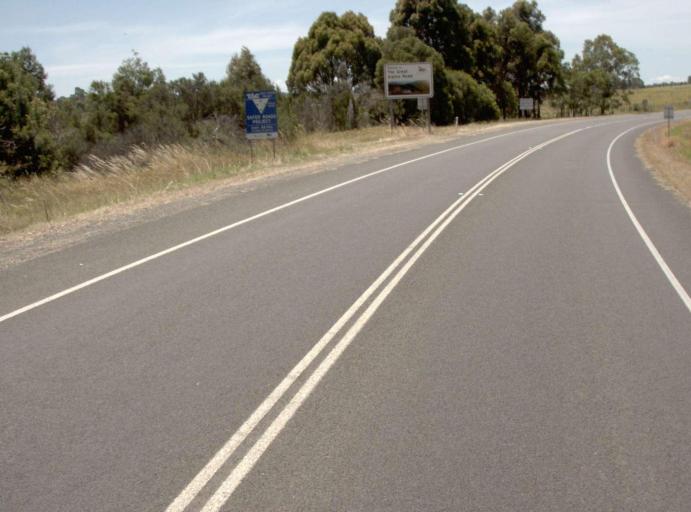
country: AU
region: Victoria
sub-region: East Gippsland
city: Bairnsdale
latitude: -37.8072
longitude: 147.6493
